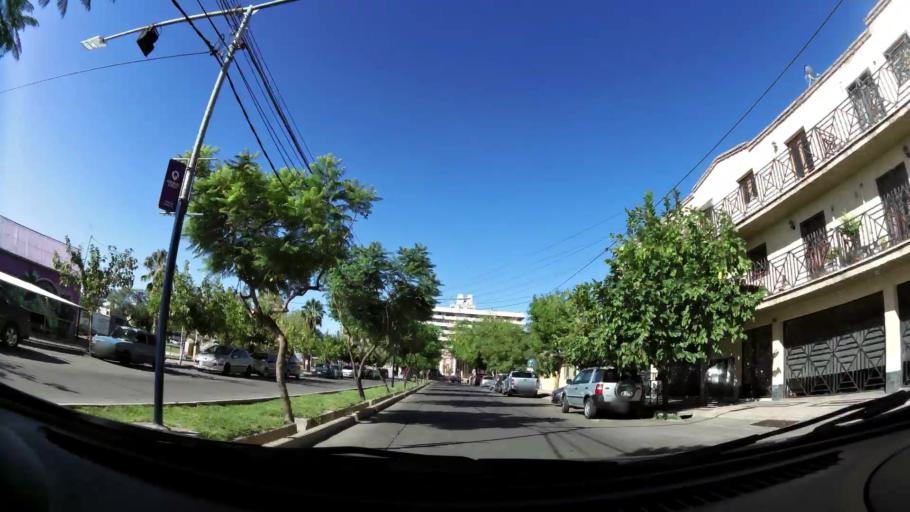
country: AR
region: Mendoza
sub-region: Departamento de Godoy Cruz
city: Godoy Cruz
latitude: -32.9241
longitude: -68.8428
